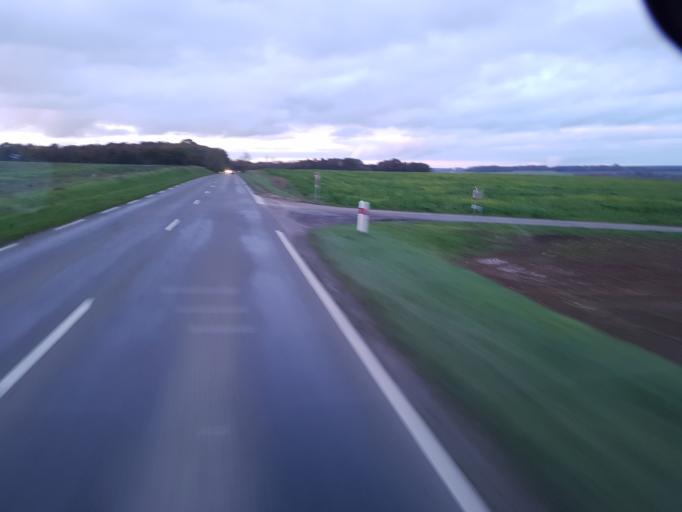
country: FR
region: Picardie
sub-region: Departement de l'Aisne
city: Coincy
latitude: 49.1674
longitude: 3.3769
